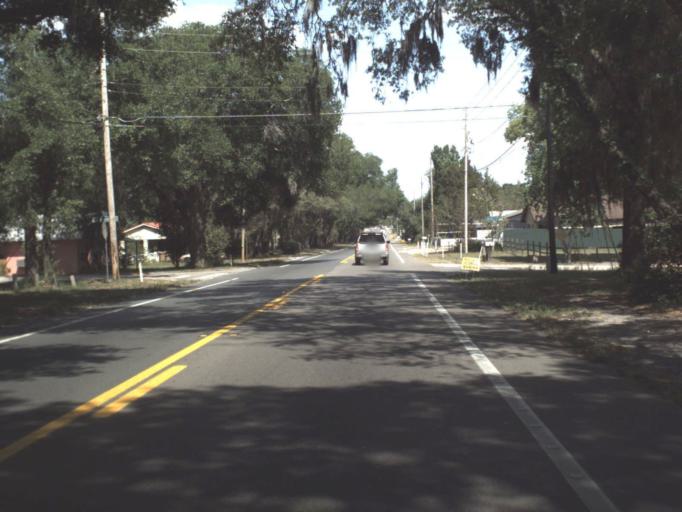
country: US
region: Florida
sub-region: Lake County
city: Mount Plymouth
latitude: 28.8078
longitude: -81.5667
